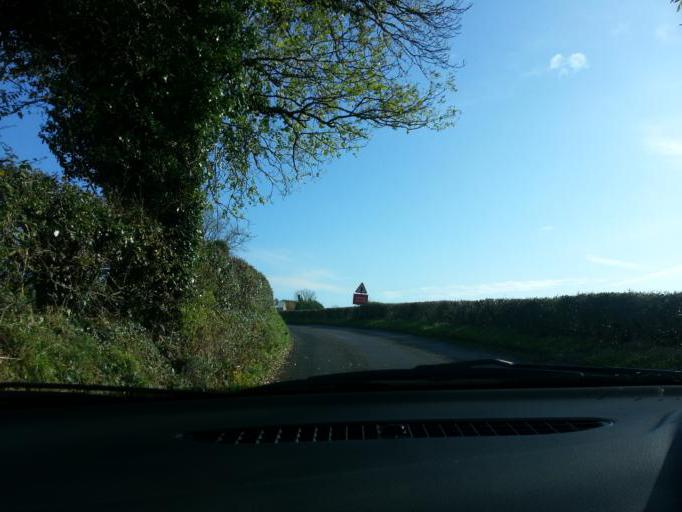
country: GB
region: Northern Ireland
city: Lisnaskea
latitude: 54.2468
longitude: -7.4178
